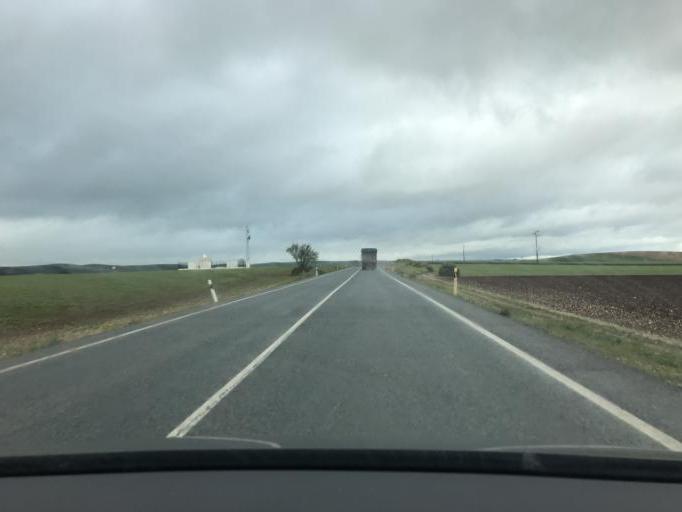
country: ES
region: Andalusia
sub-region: Provincia de Sevilla
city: Marchena
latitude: 37.3715
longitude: -5.3497
